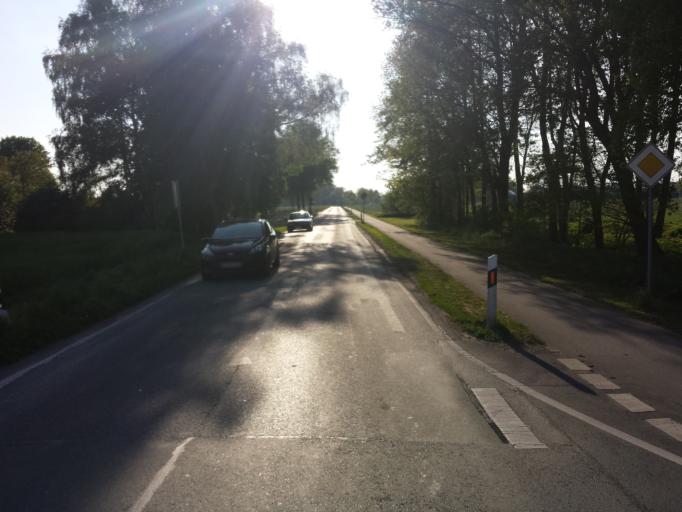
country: DE
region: North Rhine-Westphalia
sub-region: Regierungsbezirk Detmold
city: Guetersloh
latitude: 51.8498
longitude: 8.3639
